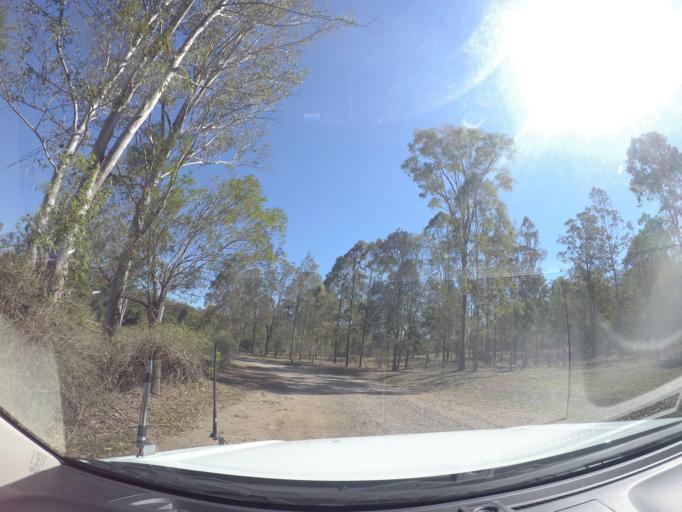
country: AU
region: Queensland
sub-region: Ipswich
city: Springfield Lakes
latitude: -27.7476
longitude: 152.8996
